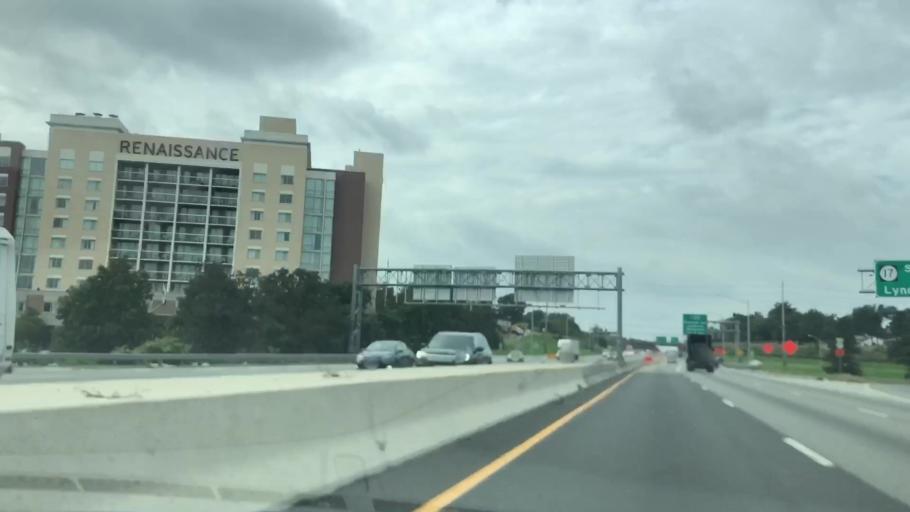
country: US
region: New Jersey
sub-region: Bergen County
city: Rutherford
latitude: 40.8116
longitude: -74.1028
